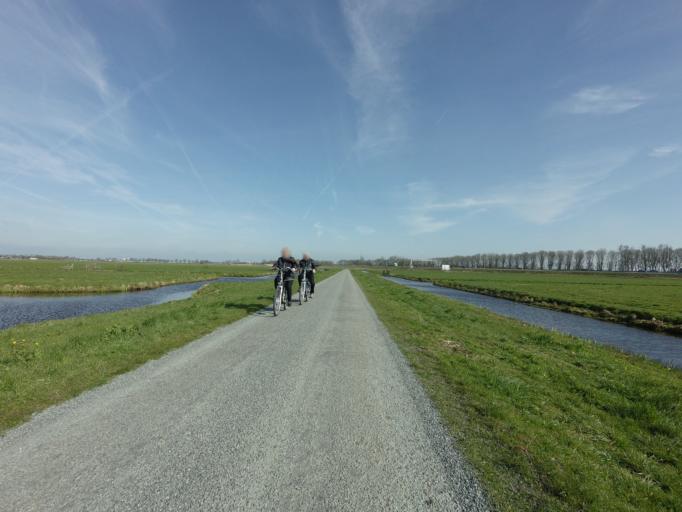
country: NL
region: South Holland
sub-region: Bodegraven-Reeuwijk
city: Bodegraven
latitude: 52.0668
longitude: 4.8141
